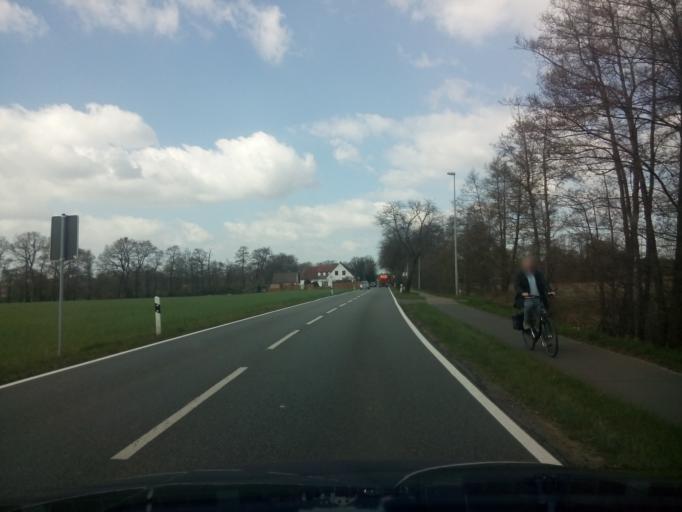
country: DE
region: Lower Saxony
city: Lilienthal
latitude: 53.1654
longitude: 8.9276
